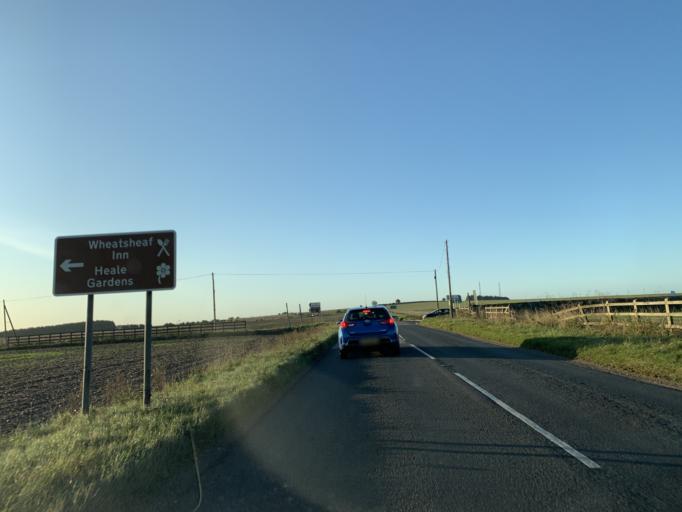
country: GB
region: England
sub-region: Wiltshire
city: Woodford
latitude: 51.1289
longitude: -1.8564
